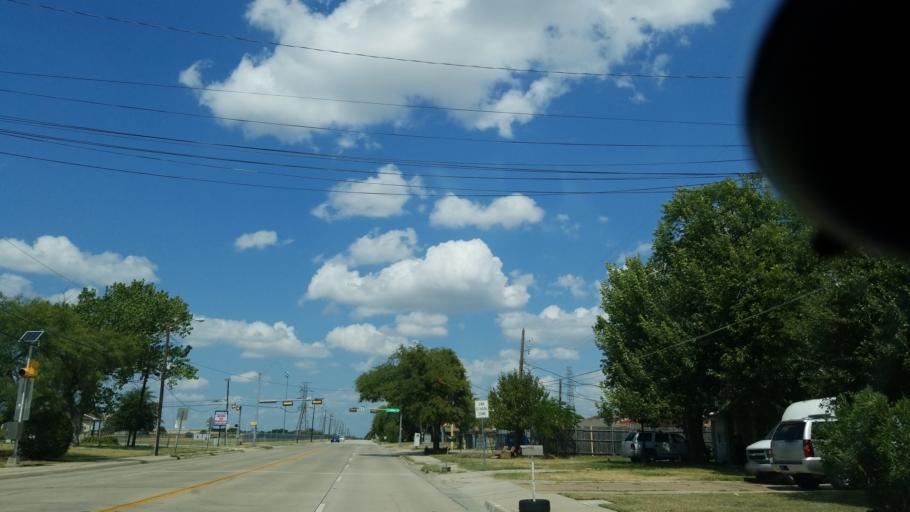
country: US
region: Texas
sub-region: Dallas County
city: Grand Prairie
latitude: 32.7197
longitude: -96.9858
